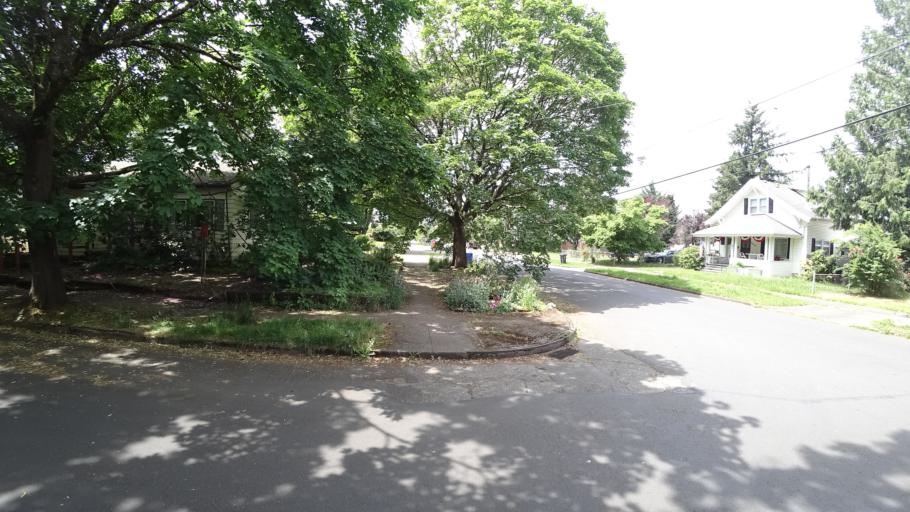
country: US
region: Oregon
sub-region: Multnomah County
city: Lents
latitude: 45.4782
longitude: -122.5913
